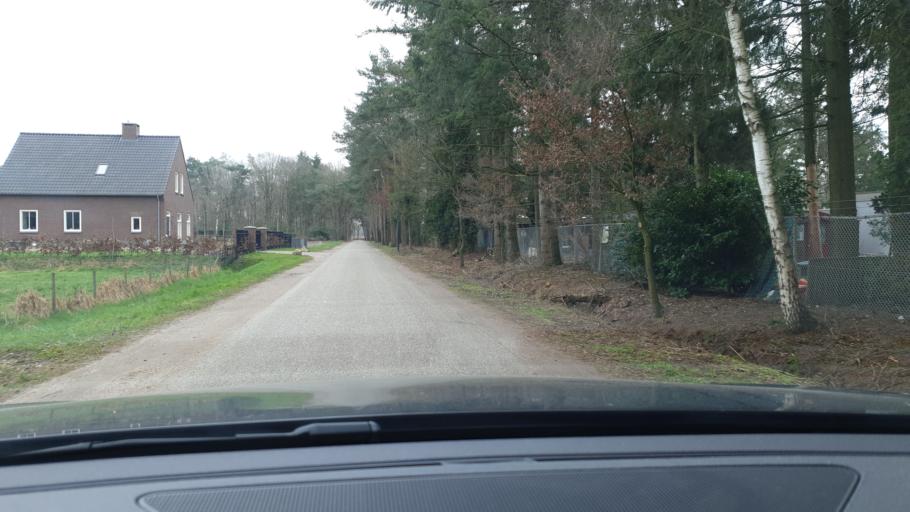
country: NL
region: North Brabant
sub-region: Gemeente Oirschot
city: Middelbeers
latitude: 51.4179
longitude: 5.2727
